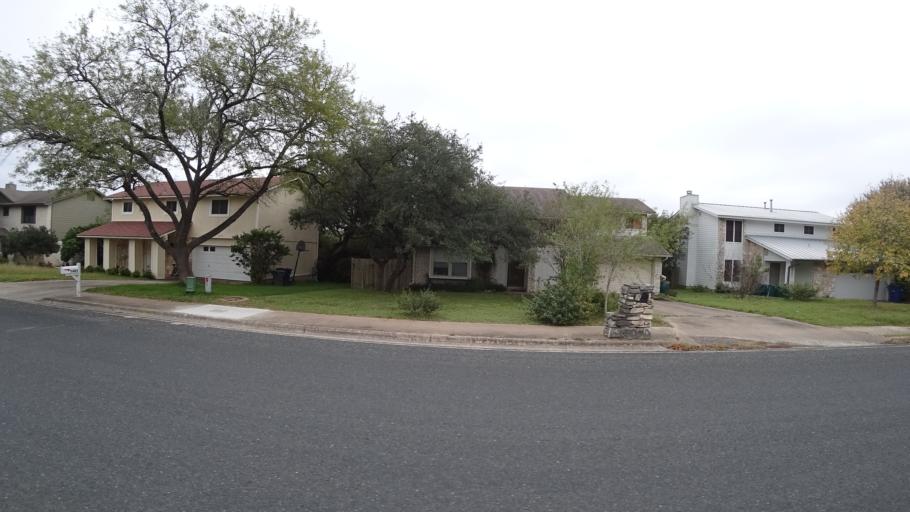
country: US
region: Texas
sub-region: Travis County
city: Barton Creek
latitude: 30.2372
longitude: -97.8938
